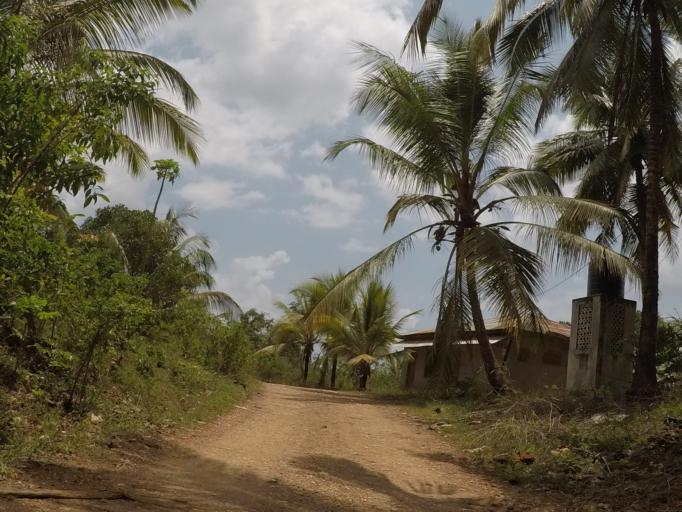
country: TZ
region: Zanzibar Central/South
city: Koani
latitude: -6.1920
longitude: 39.3070
